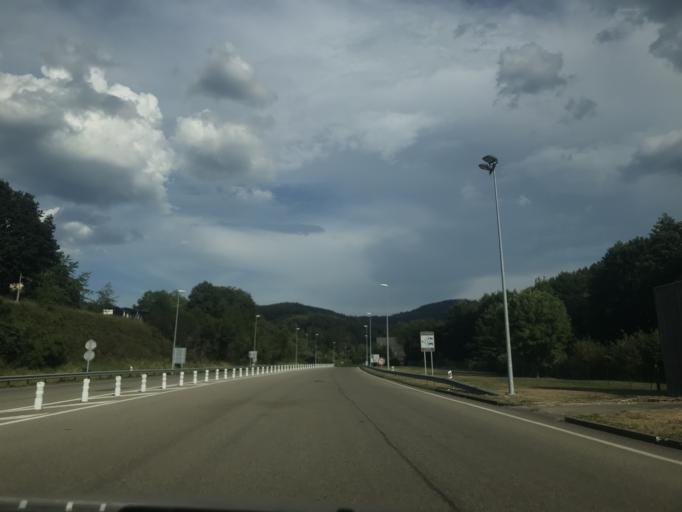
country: FR
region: Lorraine
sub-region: Departement des Vosges
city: Ban-de-Laveline
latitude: 48.2899
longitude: 7.1119
